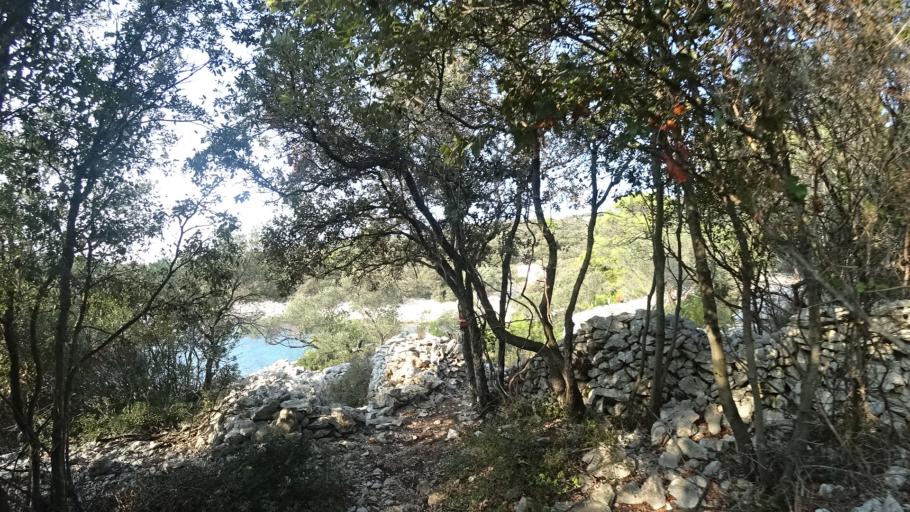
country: HR
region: Primorsko-Goranska
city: Mali Losinj
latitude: 44.5104
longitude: 14.4827
